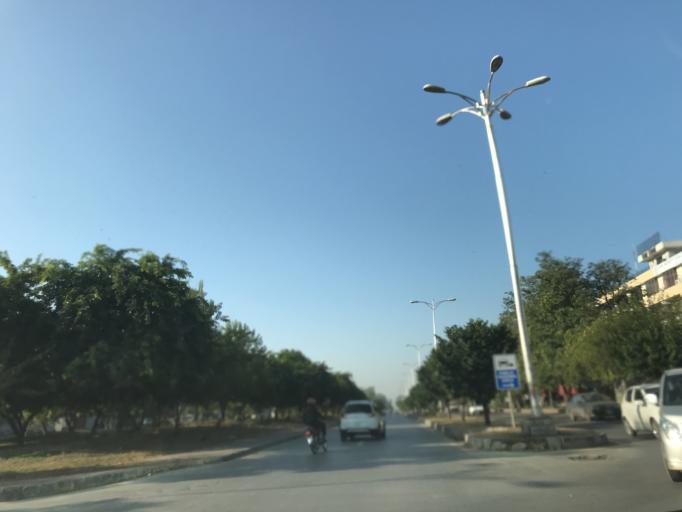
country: PK
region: Islamabad
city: Islamabad
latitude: 33.7206
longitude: 73.0793
